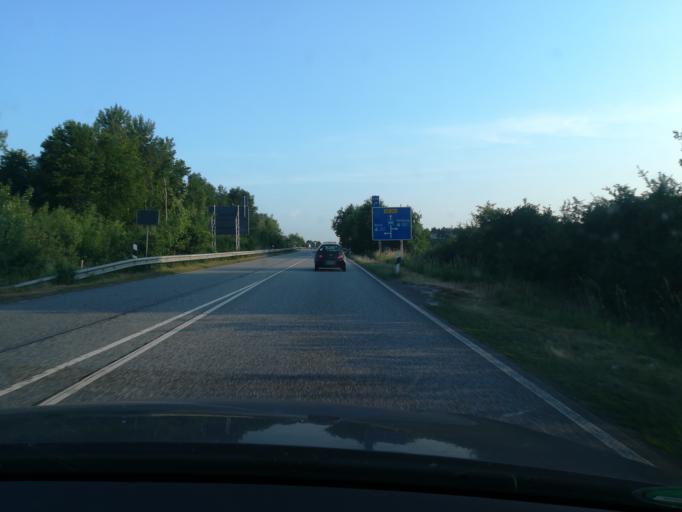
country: DE
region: Schleswig-Holstein
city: Kasseburg
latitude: 53.5566
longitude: 10.4122
